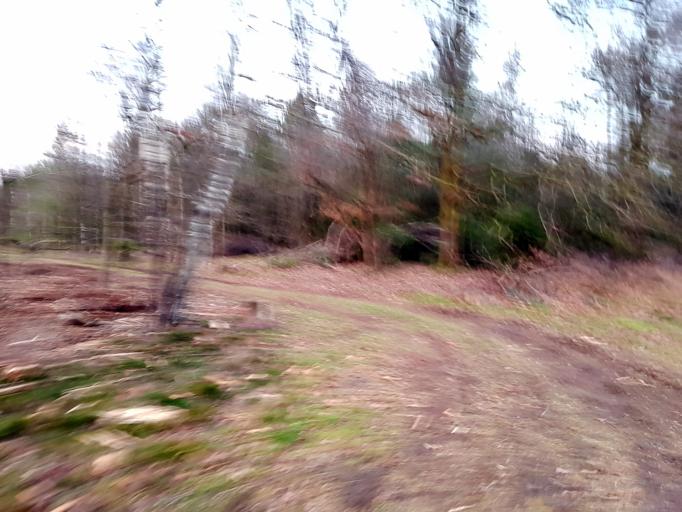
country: NL
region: Utrecht
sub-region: Gemeente Utrechtse Heuvelrug
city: Maarsbergen
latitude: 52.0544
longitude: 5.3906
